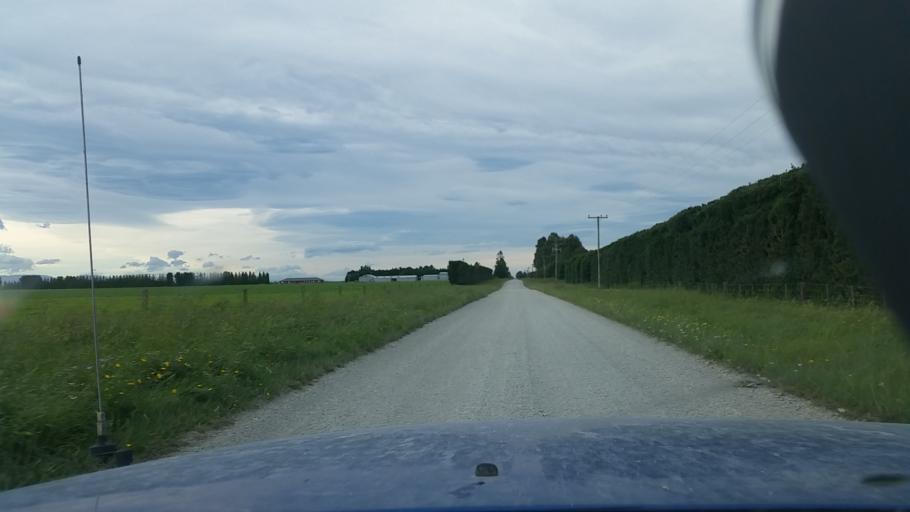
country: NZ
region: Canterbury
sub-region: Ashburton District
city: Tinwald
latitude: -43.8627
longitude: 171.5291
